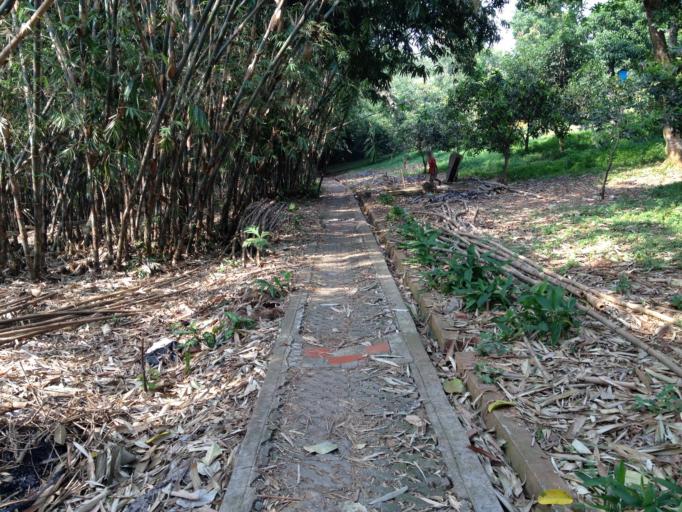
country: ID
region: West Java
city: Pamulang
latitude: -6.3148
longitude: 106.7795
